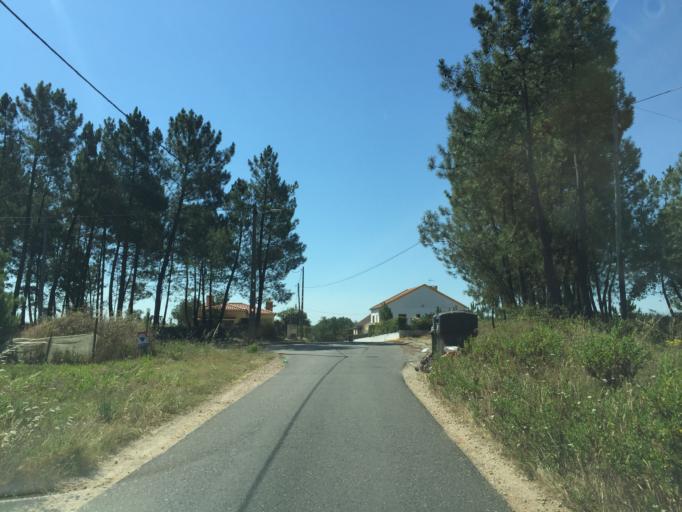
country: PT
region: Santarem
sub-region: Ferreira do Zezere
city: Ferreira do Zezere
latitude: 39.5954
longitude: -8.2929
